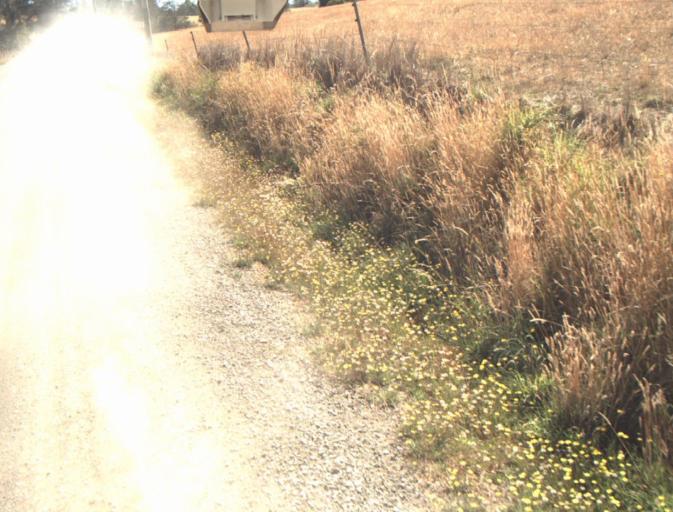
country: AU
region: Tasmania
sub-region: Launceston
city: Mayfield
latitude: -41.2254
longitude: 147.2368
